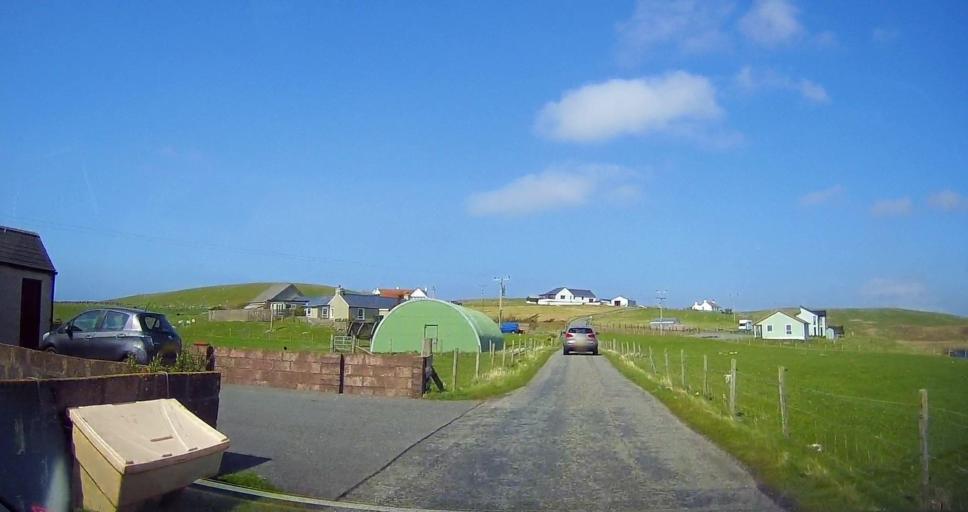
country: GB
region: Scotland
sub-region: Shetland Islands
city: Sandwick
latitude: 60.0667
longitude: -1.3378
